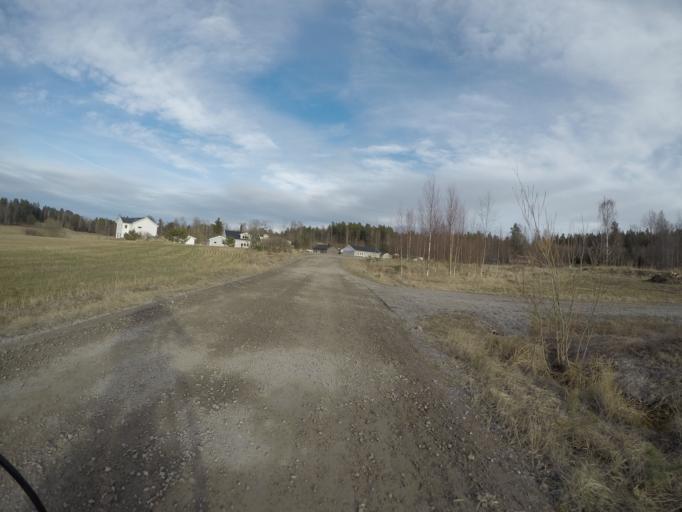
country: SE
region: Soedermanland
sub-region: Eskilstuna Kommun
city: Hallbybrunn
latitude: 59.4298
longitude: 16.4170
